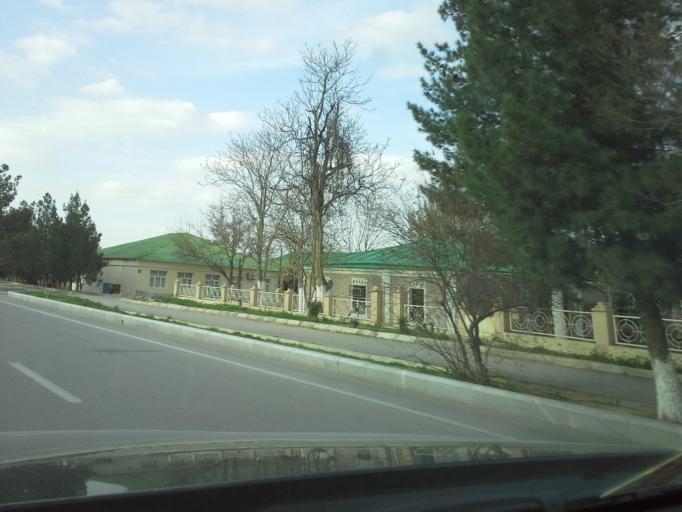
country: TM
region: Ahal
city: Abadan
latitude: 37.9609
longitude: 58.2236
